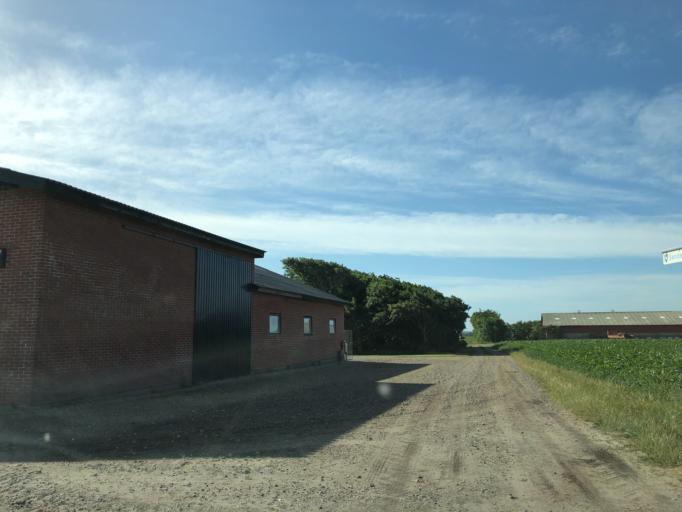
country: DK
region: Central Jutland
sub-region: Holstebro Kommune
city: Ulfborg
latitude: 56.3339
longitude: 8.3031
